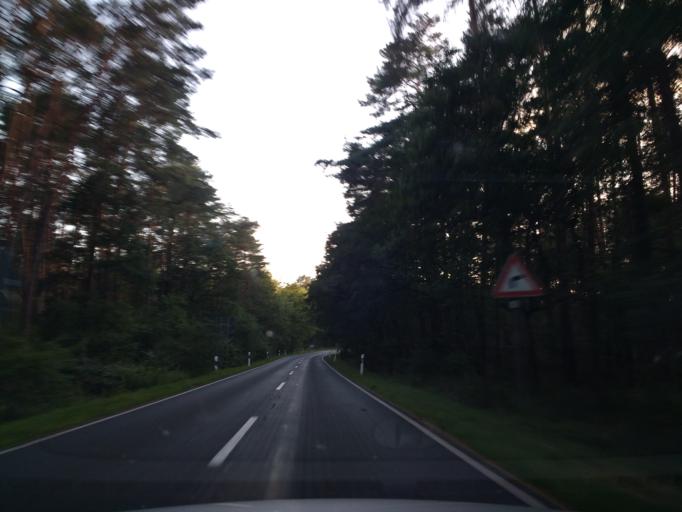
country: DE
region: Lower Saxony
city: Neustadt am Rubenberge
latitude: 52.5380
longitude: 9.3867
